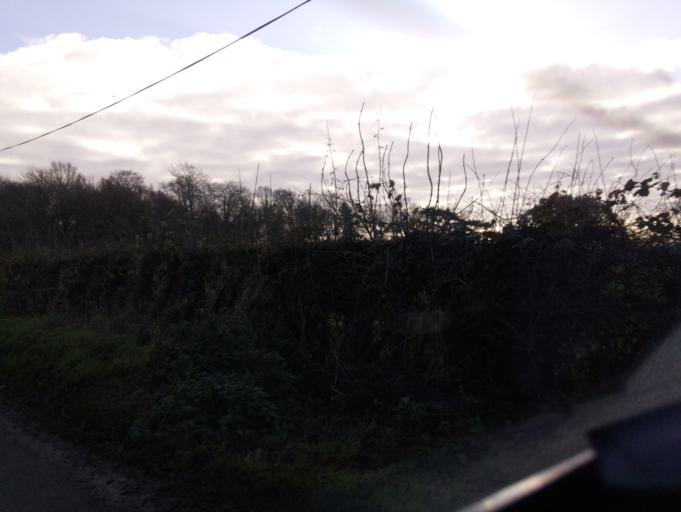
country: GB
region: England
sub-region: Staffordshire
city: Barton under Needwood
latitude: 52.8014
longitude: -1.7192
